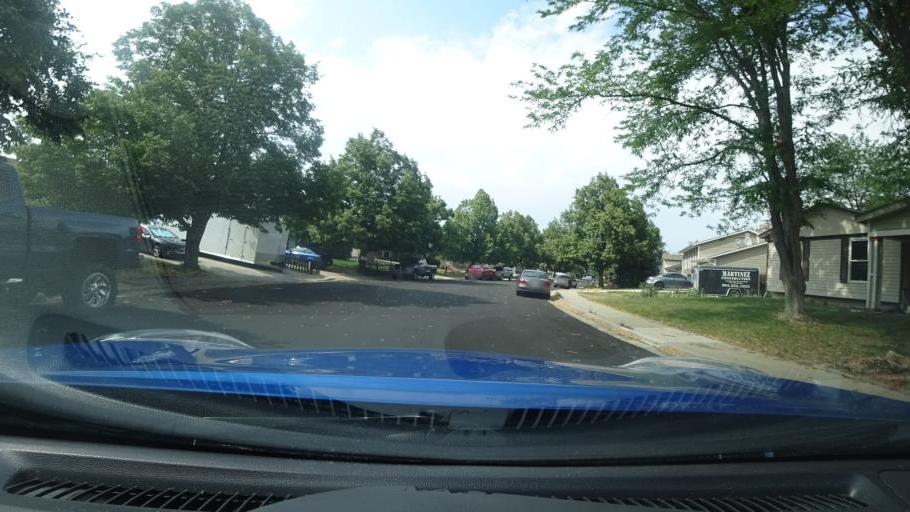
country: US
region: Colorado
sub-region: Adams County
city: Aurora
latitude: 39.6889
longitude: -104.7847
